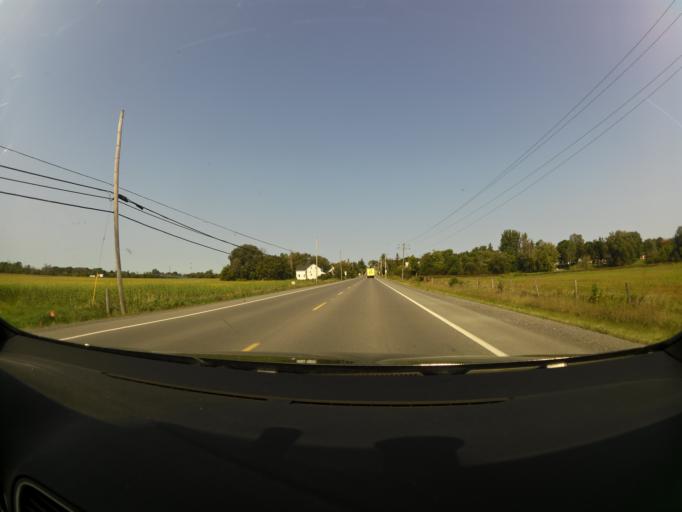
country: CA
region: Ontario
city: Bells Corners
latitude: 45.3406
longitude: -76.0309
